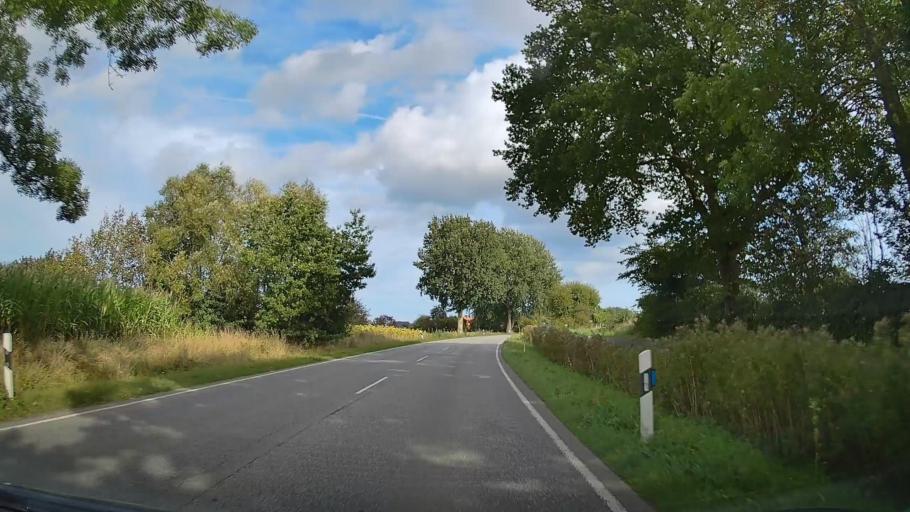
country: DE
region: Schleswig-Holstein
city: Gelting
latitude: 54.7466
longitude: 9.8875
